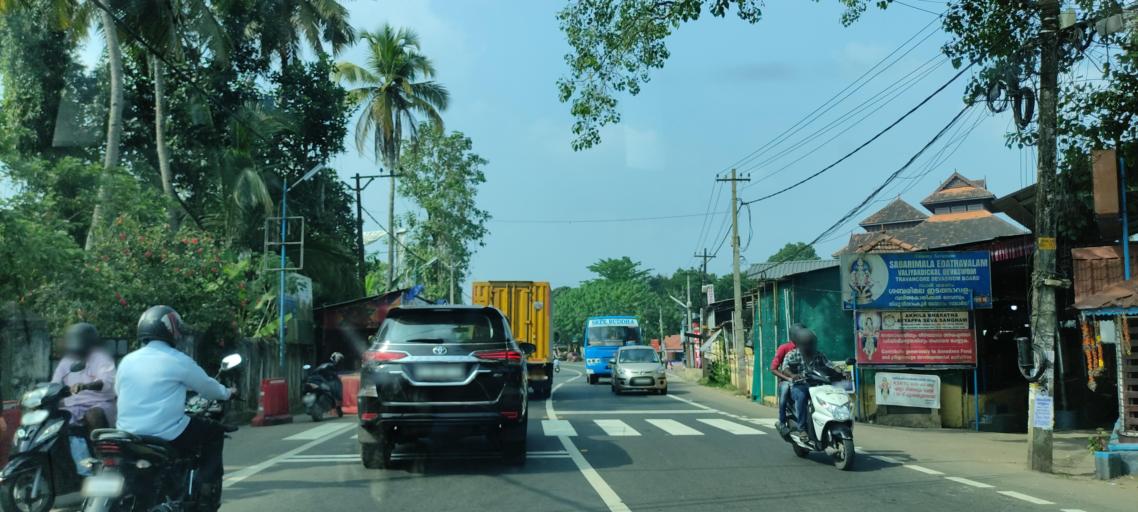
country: IN
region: Kerala
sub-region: Pattanamtitta
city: Adur
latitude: 9.2322
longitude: 76.6748
